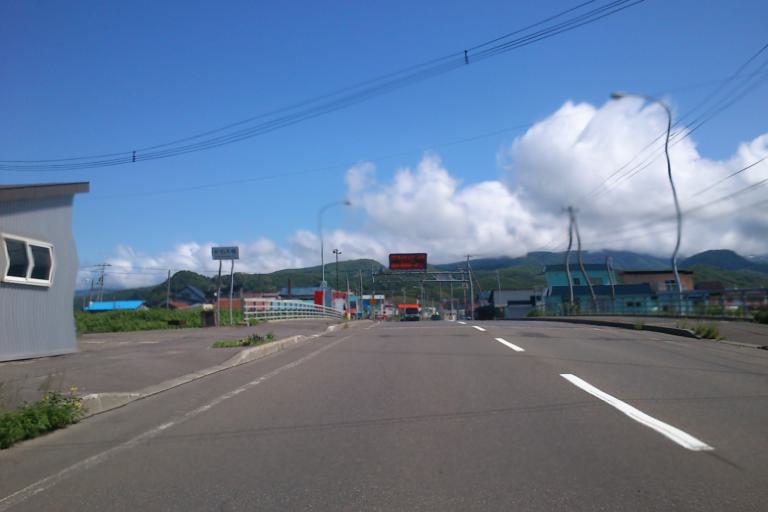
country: JP
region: Hokkaido
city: Ishikari
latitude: 43.5759
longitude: 141.3864
